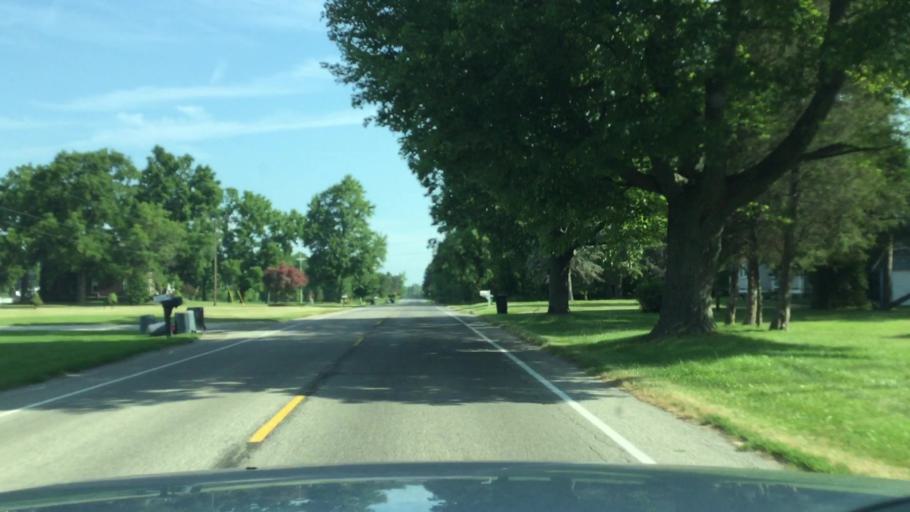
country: US
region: Michigan
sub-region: Genesee County
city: Flushing
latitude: 43.1109
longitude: -83.8728
